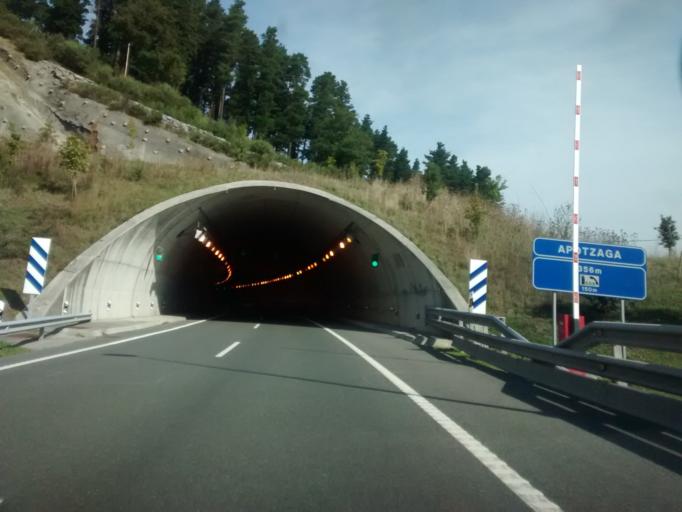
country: ES
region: Basque Country
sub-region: Provincia de Guipuzcoa
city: Aretxabaleta
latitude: 43.0331
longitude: -2.5097
